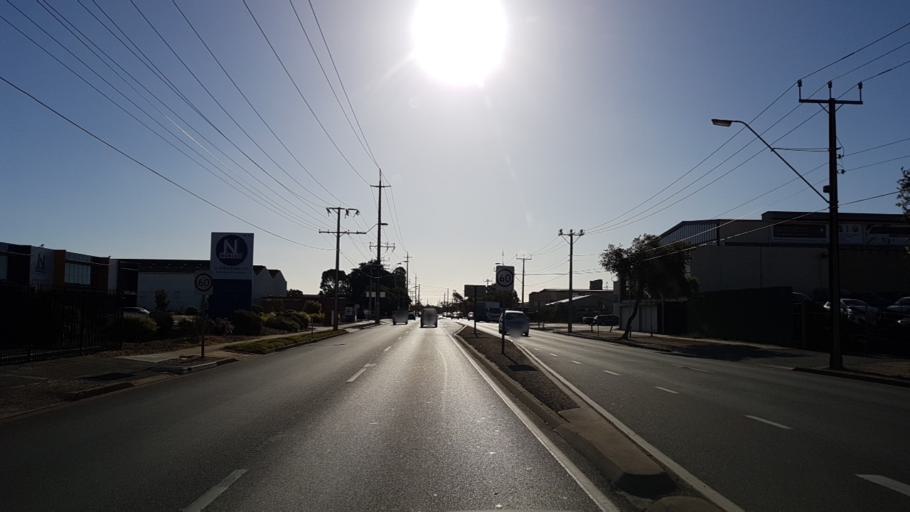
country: AU
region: South Australia
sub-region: Port Adelaide Enfield
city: Blair Athol
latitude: -34.8489
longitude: 138.5875
